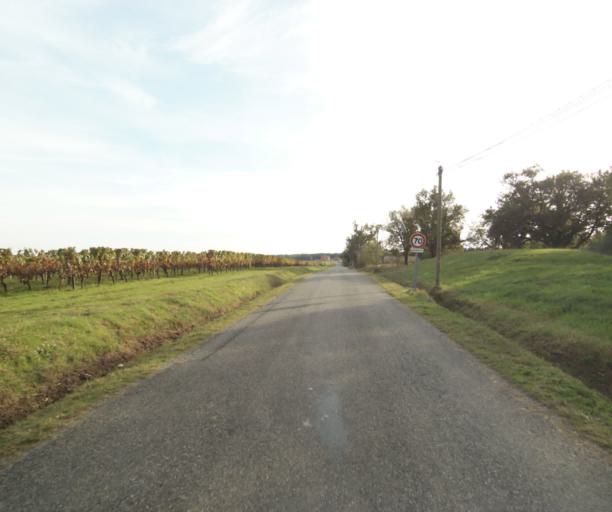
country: FR
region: Midi-Pyrenees
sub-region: Departement du Tarn-et-Garonne
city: Campsas
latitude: 43.8900
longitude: 1.3258
